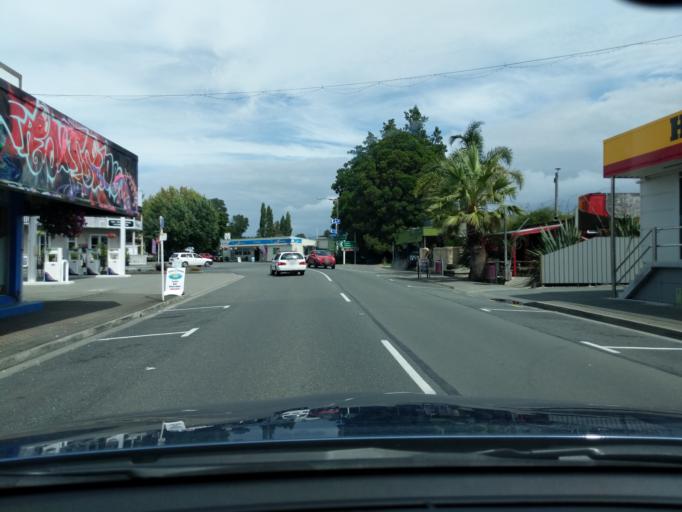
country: NZ
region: Tasman
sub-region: Tasman District
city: Takaka
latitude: -40.8604
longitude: 172.8059
